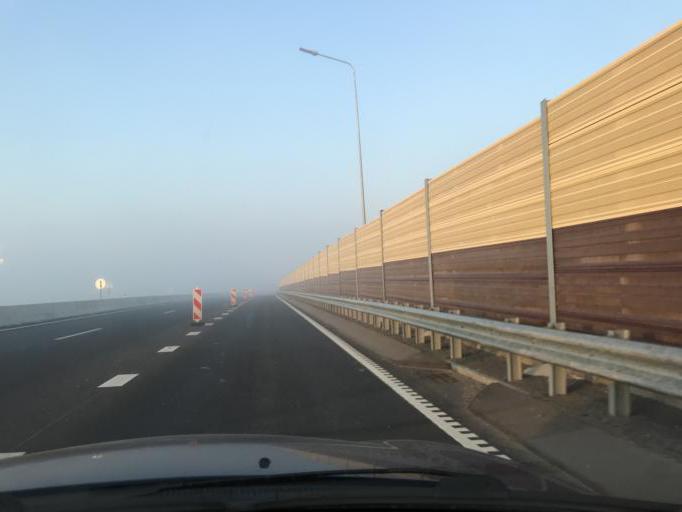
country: BY
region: Minsk
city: Ivyanyets
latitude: 54.0462
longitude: 26.7367
